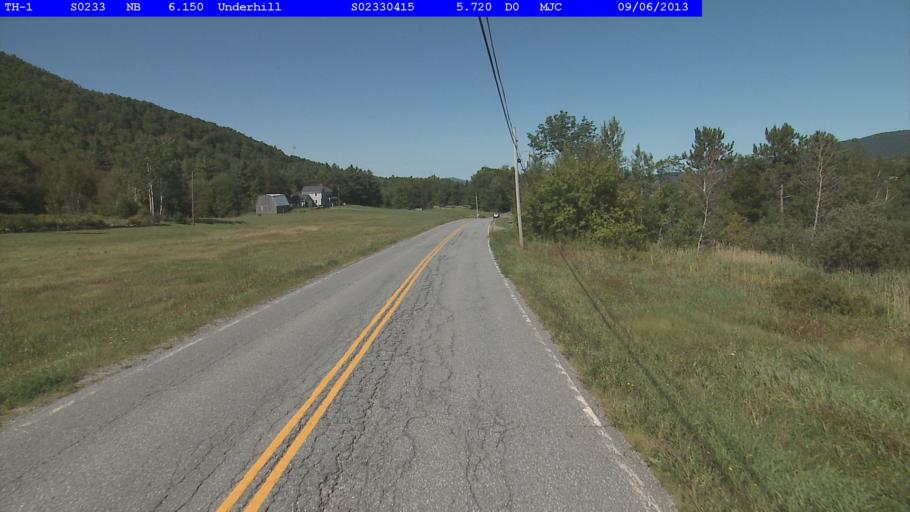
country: US
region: Vermont
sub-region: Chittenden County
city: Jericho
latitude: 44.5474
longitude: -72.8679
